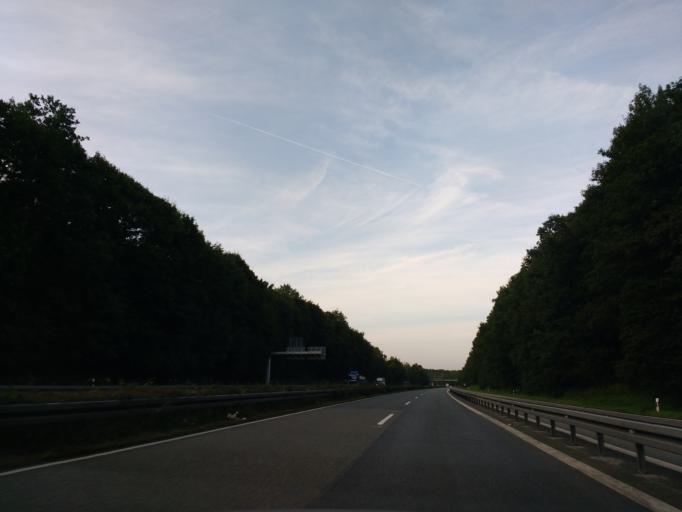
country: DE
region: North Rhine-Westphalia
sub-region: Regierungsbezirk Detmold
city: Wunnenberg
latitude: 51.5844
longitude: 8.7214
